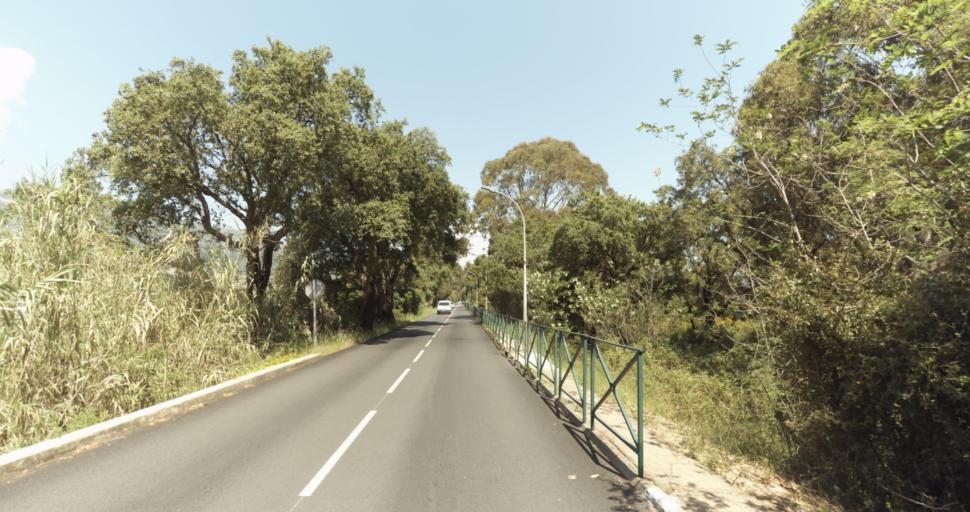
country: FR
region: Corsica
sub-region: Departement de la Haute-Corse
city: Biguglia
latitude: 42.5993
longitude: 9.4354
